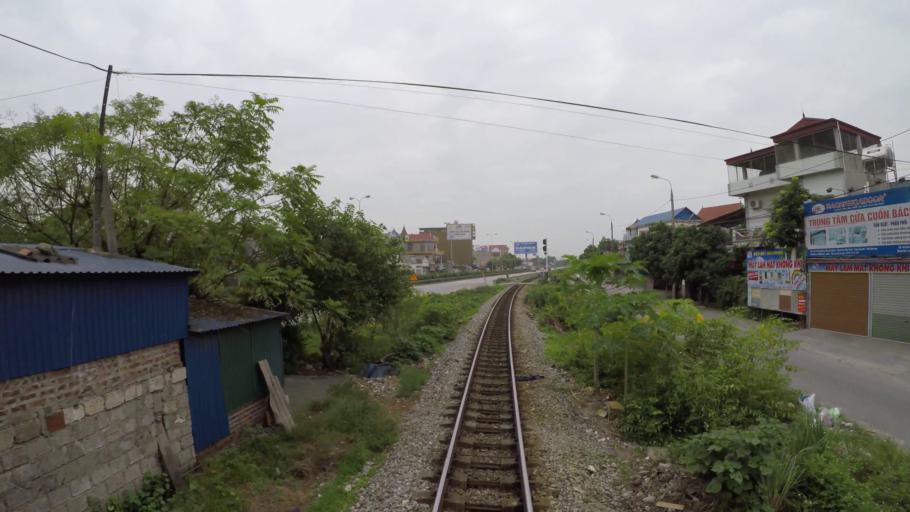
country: VN
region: Hai Duong
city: Phu Thai
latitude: 20.9671
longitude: 106.5055
